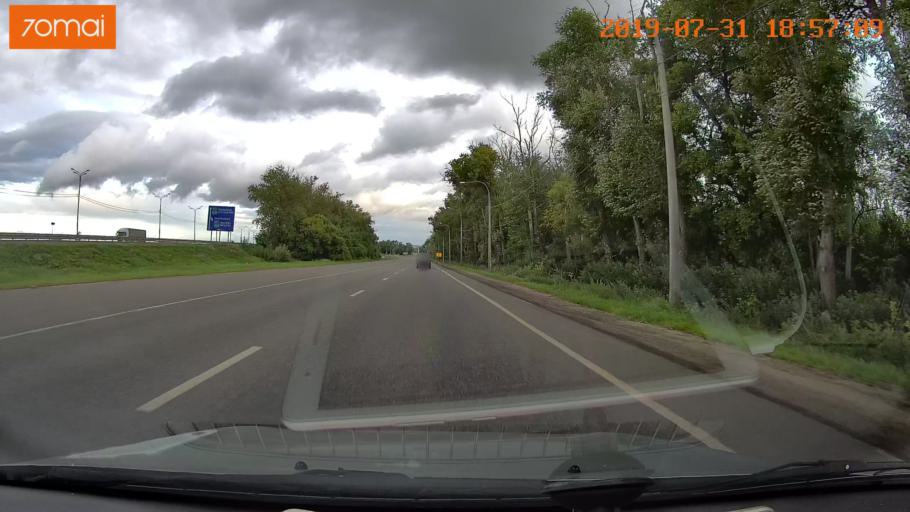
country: RU
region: Moskovskaya
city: Raduzhnyy
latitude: 55.1566
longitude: 38.6881
